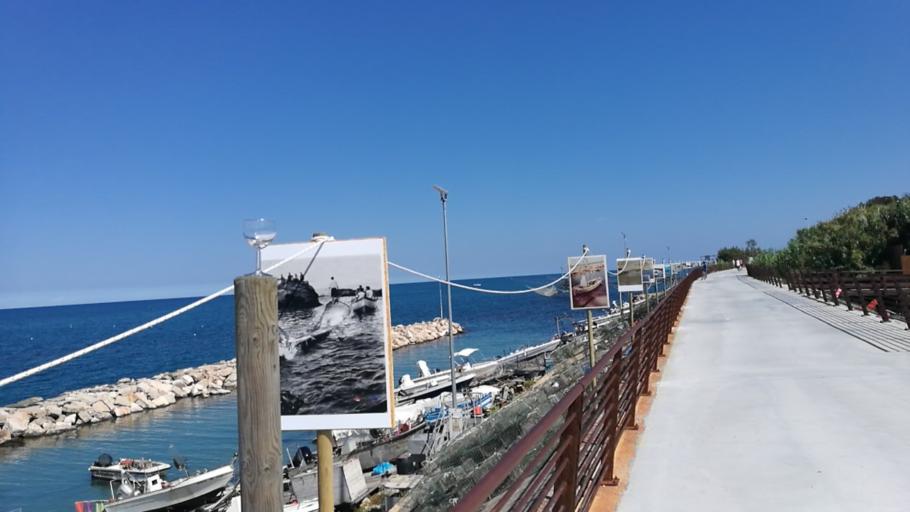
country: IT
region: Abruzzo
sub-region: Provincia di Chieti
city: Fossacesia
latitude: 42.2672
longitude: 14.5013
